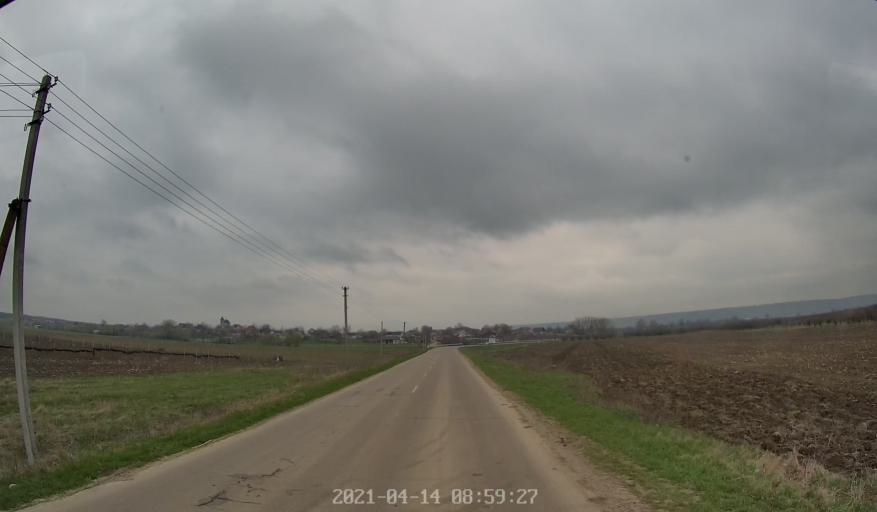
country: MD
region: Chisinau
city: Vadul lui Voda
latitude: 47.1003
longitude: 29.1046
